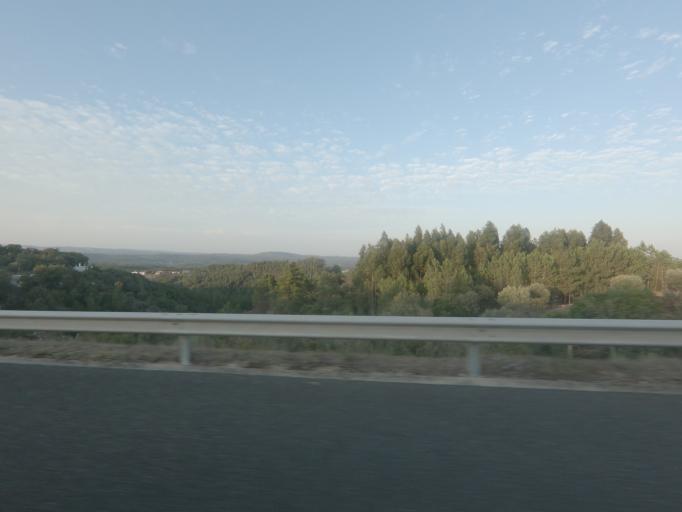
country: PT
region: Leiria
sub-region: Leiria
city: Santa Catarina da Serra
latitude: 39.6882
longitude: -8.6889
